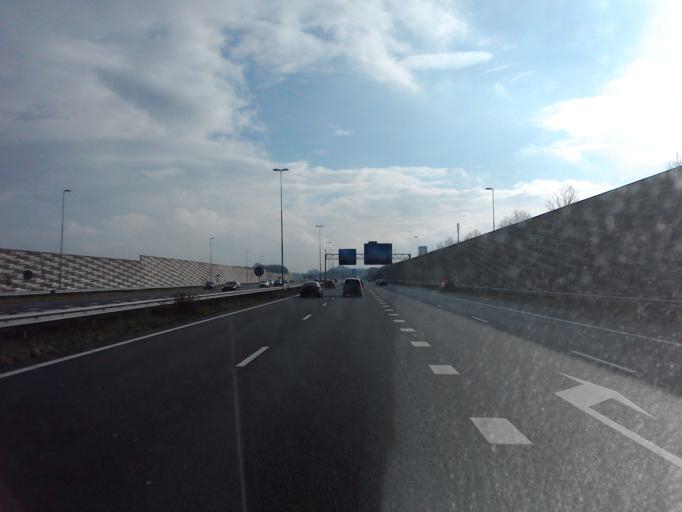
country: NL
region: North Brabant
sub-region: Gemeente 's-Hertogenbosch
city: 's-Hertogenbosch
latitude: 51.7319
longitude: 5.3124
